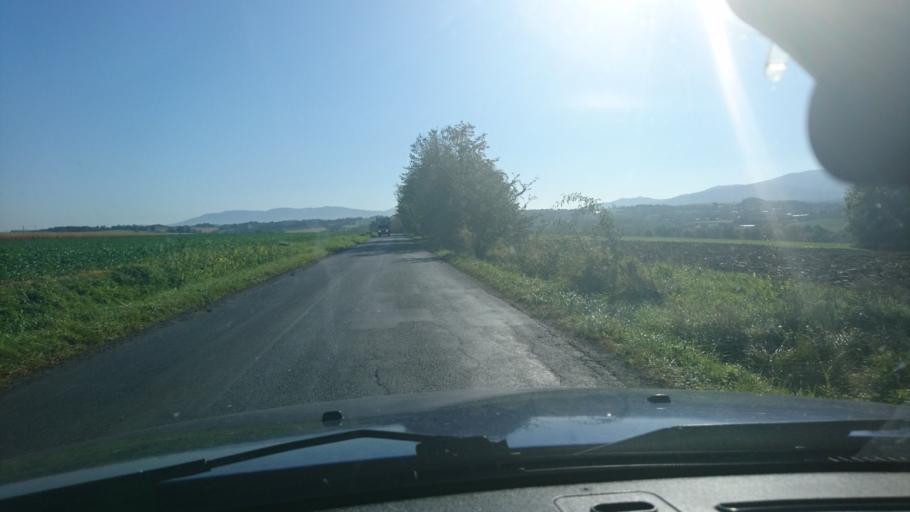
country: PL
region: Silesian Voivodeship
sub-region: Powiat bielski
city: Bronow
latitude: 49.8555
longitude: 18.9261
